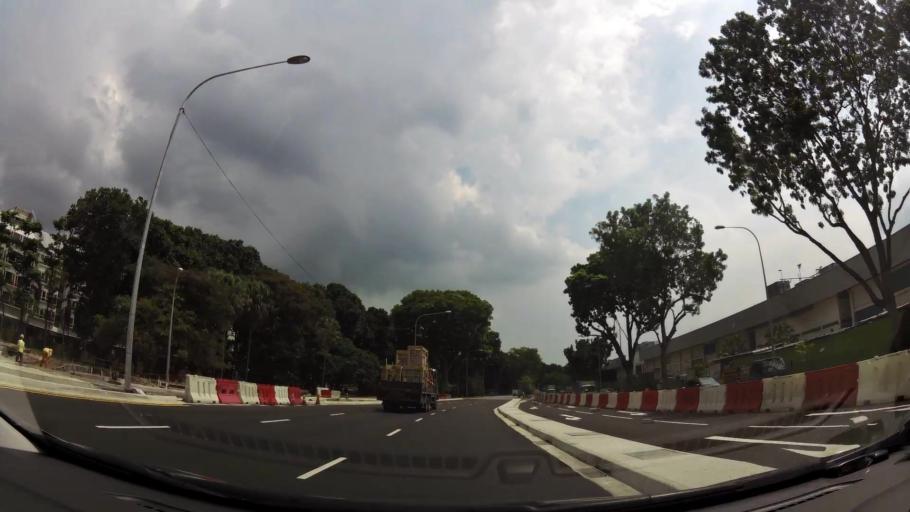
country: SG
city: Singapore
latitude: 1.2875
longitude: 103.7776
